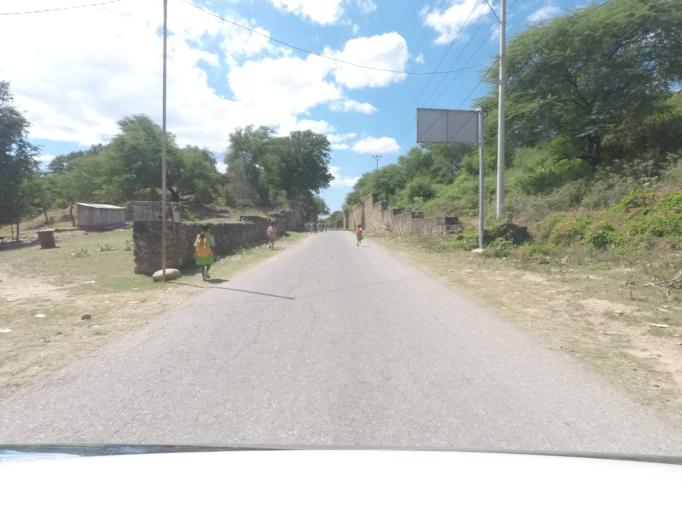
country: TL
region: Lautem
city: Lospalos
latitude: -8.3646
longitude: 126.9003
